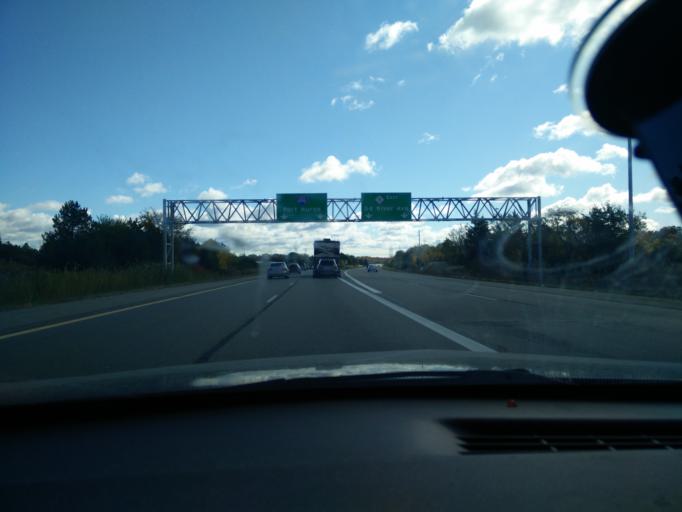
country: US
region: Michigan
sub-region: Oakland County
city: Novi
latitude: 42.4842
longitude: -83.4469
